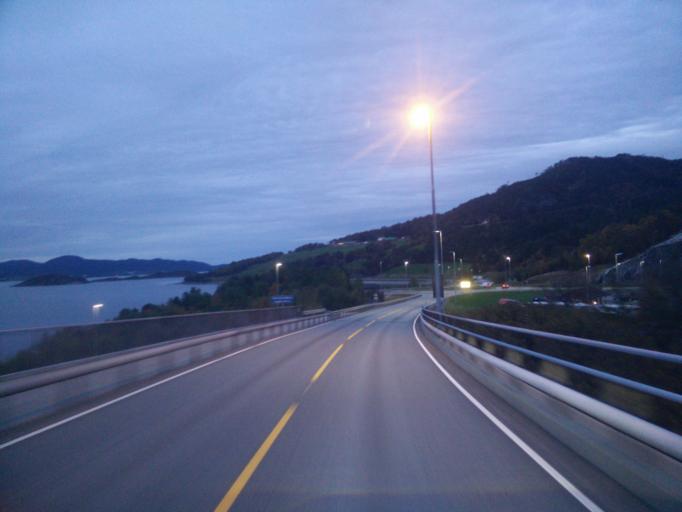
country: NO
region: More og Romsdal
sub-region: Kristiansund
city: Rensvik
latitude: 62.9747
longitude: 7.7847
